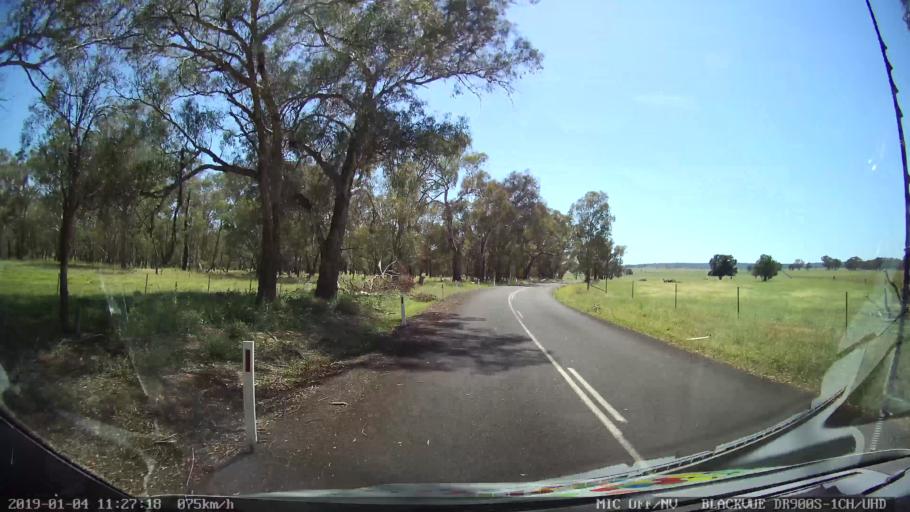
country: AU
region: New South Wales
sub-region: Cabonne
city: Molong
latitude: -33.1097
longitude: 148.7611
